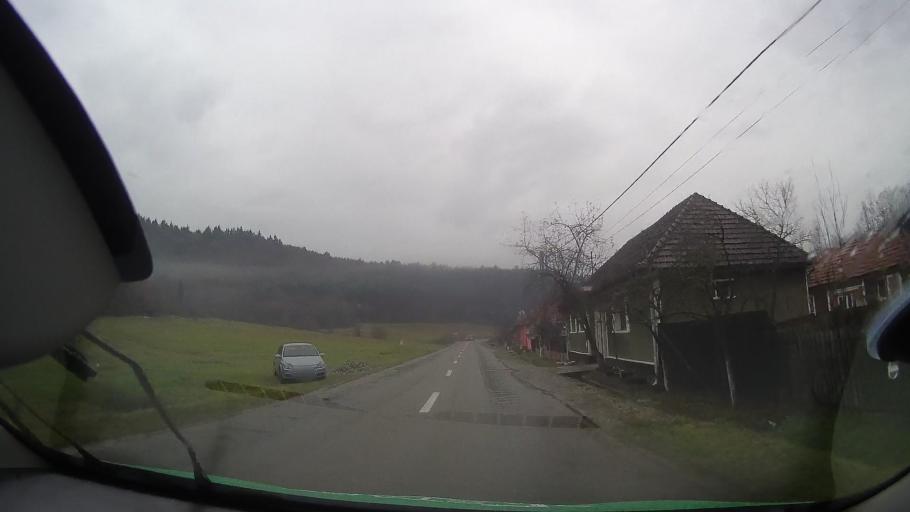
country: RO
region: Bihor
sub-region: Comuna Holod
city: Vintere
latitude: 46.7671
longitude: 22.1666
